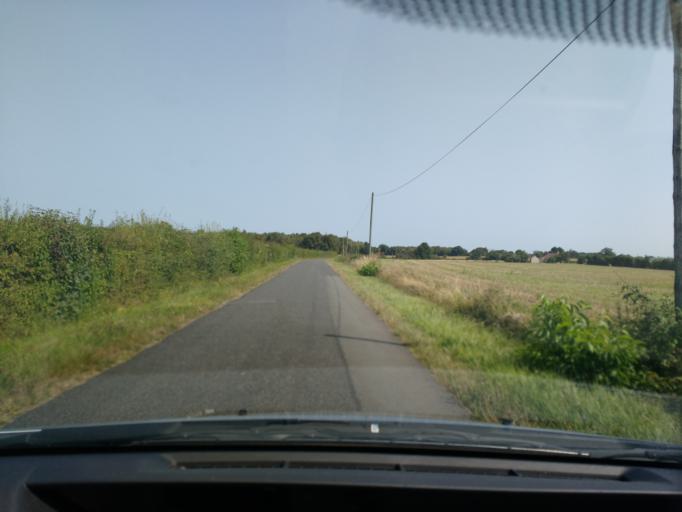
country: FR
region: Pays de la Loire
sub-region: Departement de Maine-et-Loire
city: Bauge-en-Anjou
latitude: 47.5526
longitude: -0.0348
